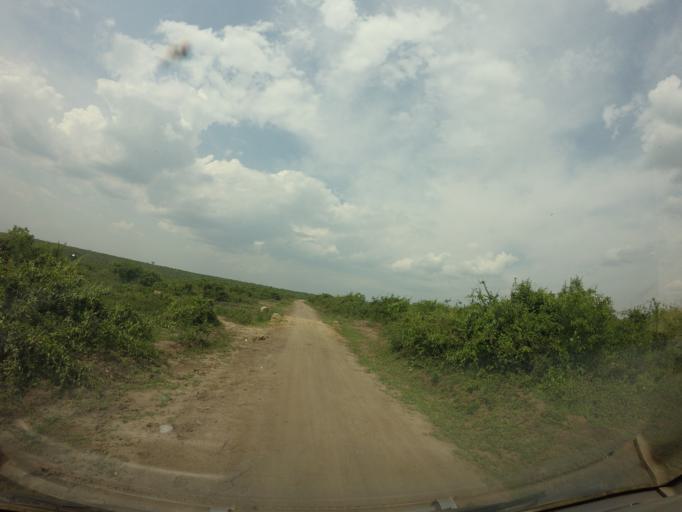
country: UG
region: Western Region
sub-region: Rubirizi District
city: Rubirizi
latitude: -0.2102
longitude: 29.9091
